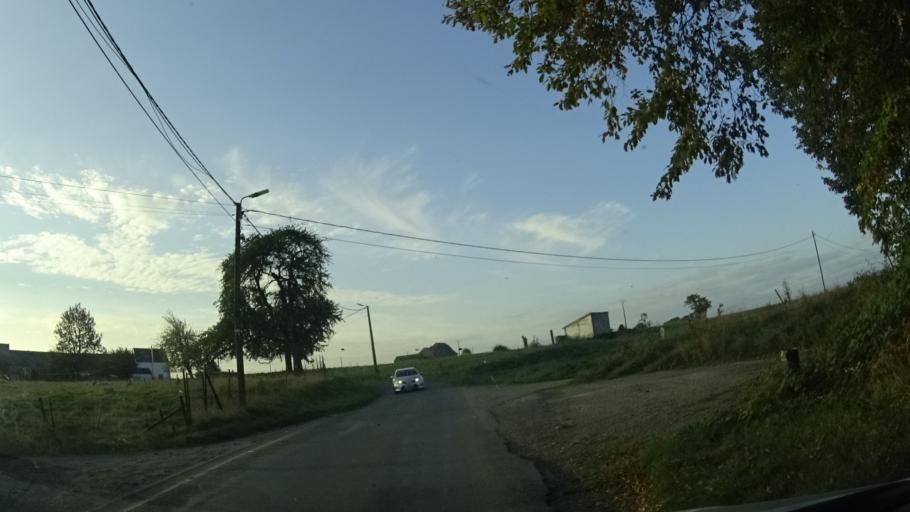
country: BE
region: Wallonia
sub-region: Province du Hainaut
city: Beaumont
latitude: 50.2487
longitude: 4.2612
